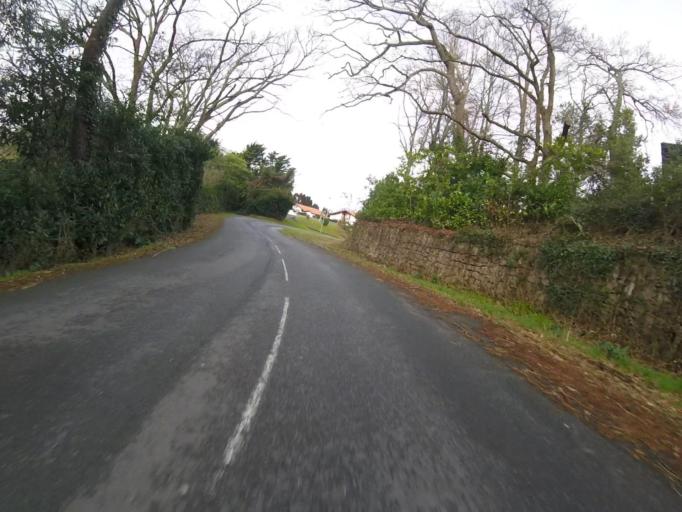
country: FR
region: Aquitaine
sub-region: Departement des Pyrenees-Atlantiques
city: Saint-Jean-de-Luz
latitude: 43.3709
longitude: -1.6584
